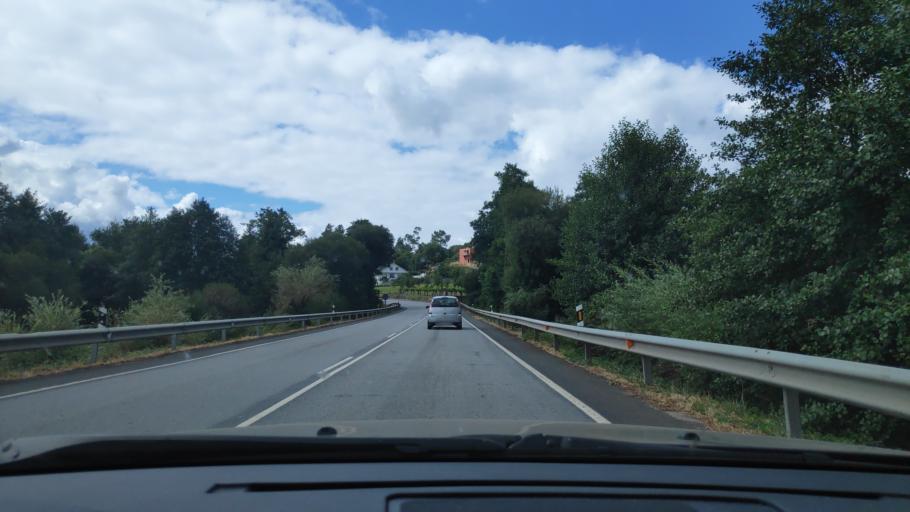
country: ES
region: Galicia
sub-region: Provincia de Pontevedra
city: Portas
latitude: 42.5916
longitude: -8.6910
